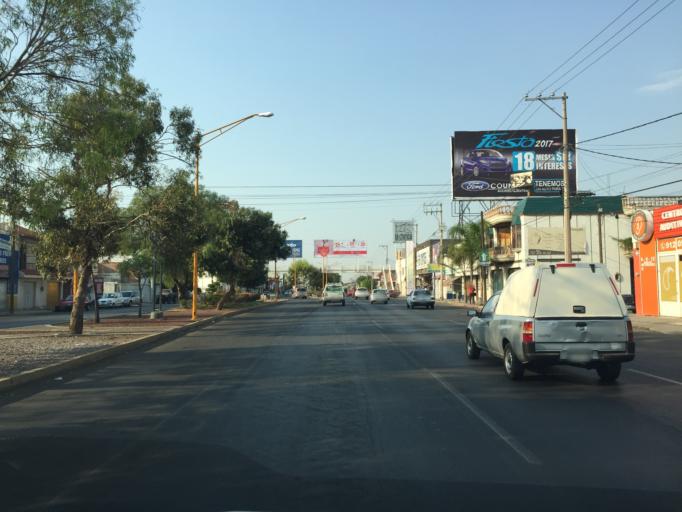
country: MX
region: Aguascalientes
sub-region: Aguascalientes
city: Pocitos
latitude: 21.8957
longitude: -102.3171
